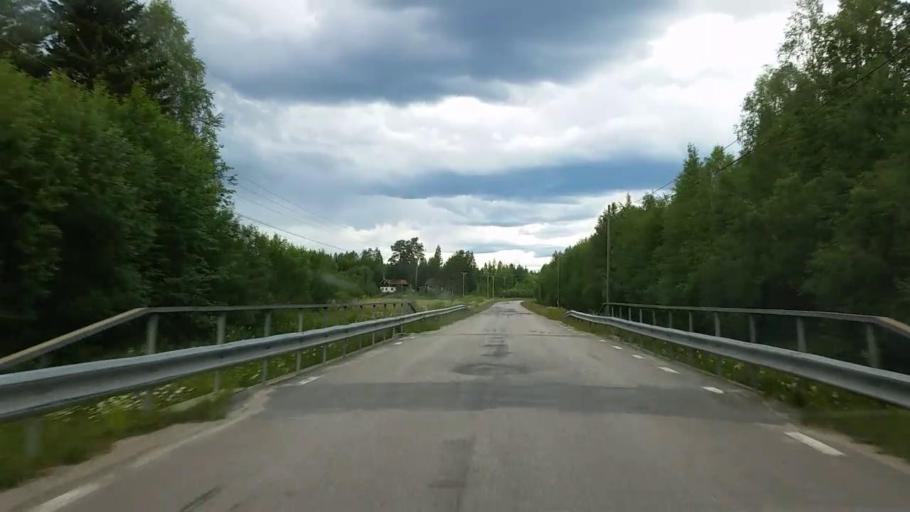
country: SE
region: Gaevleborg
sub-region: Ovanakers Kommun
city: Edsbyn
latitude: 61.4555
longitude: 15.8770
